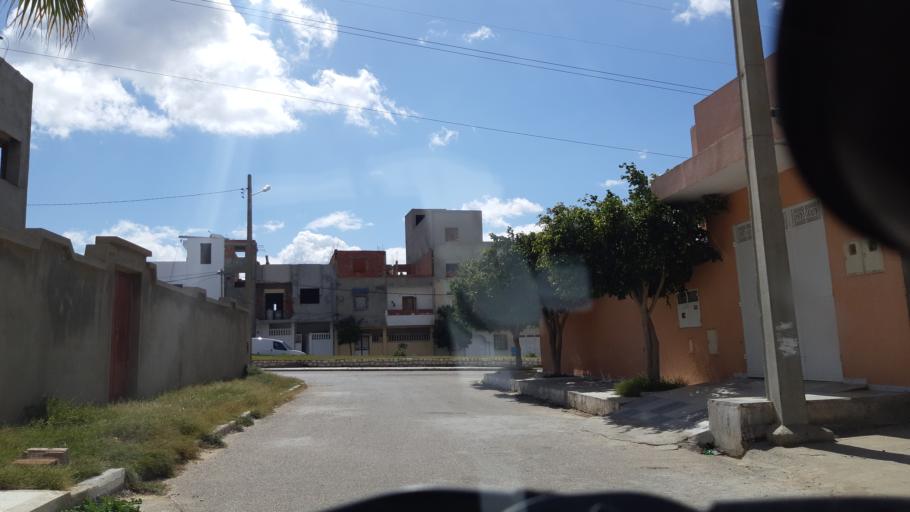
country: TN
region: Susah
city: Akouda
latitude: 35.8873
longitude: 10.5332
